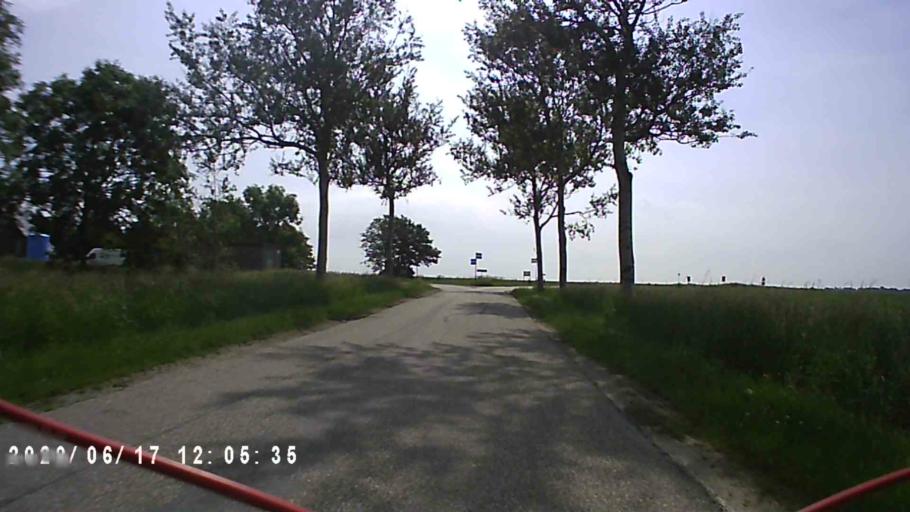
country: NL
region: Groningen
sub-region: Gemeente De Marne
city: Ulrum
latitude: 53.3363
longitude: 6.3531
